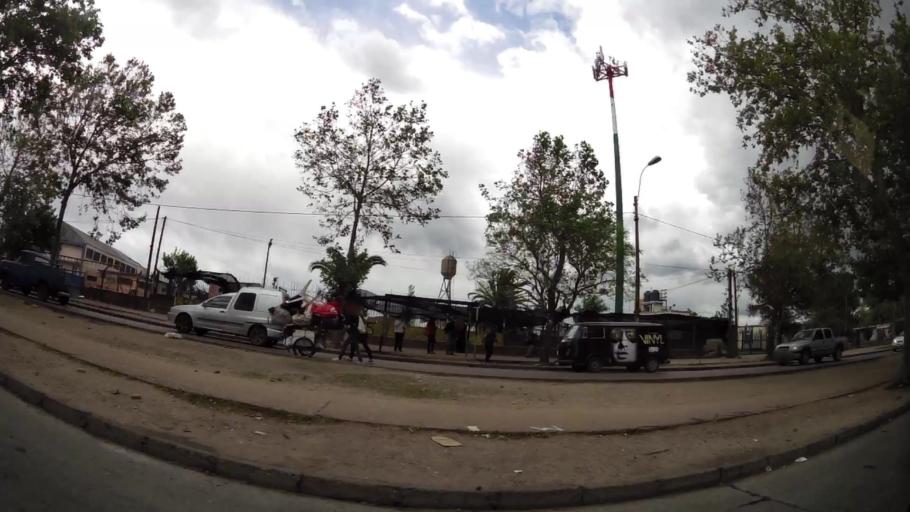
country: UY
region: Canelones
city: Toledo
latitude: -34.8219
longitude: -56.1402
